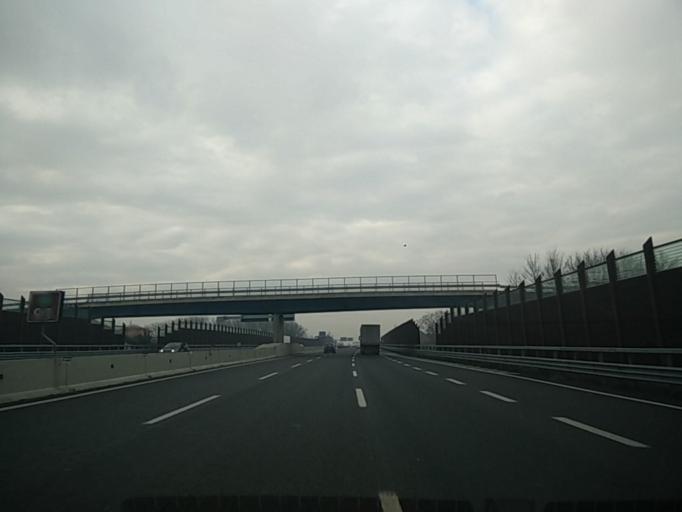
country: IT
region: Emilia-Romagna
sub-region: Provincia di Rimini
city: Santarcangelo
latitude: 44.0863
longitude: 12.4630
